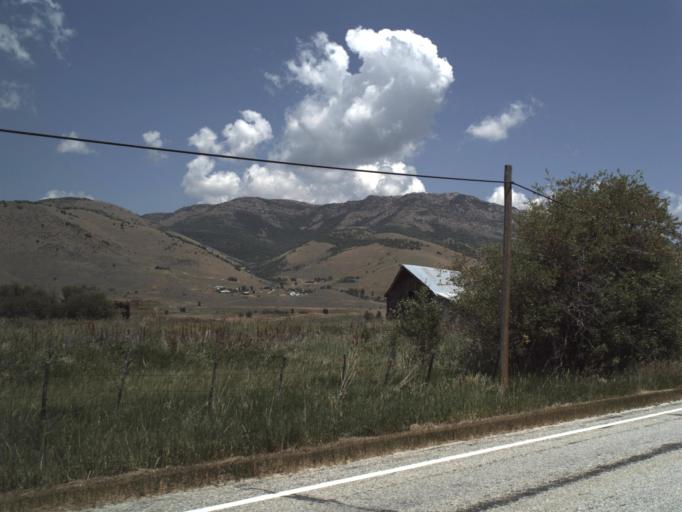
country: US
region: Utah
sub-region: Weber County
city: Wolf Creek
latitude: 41.2623
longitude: -111.7559
